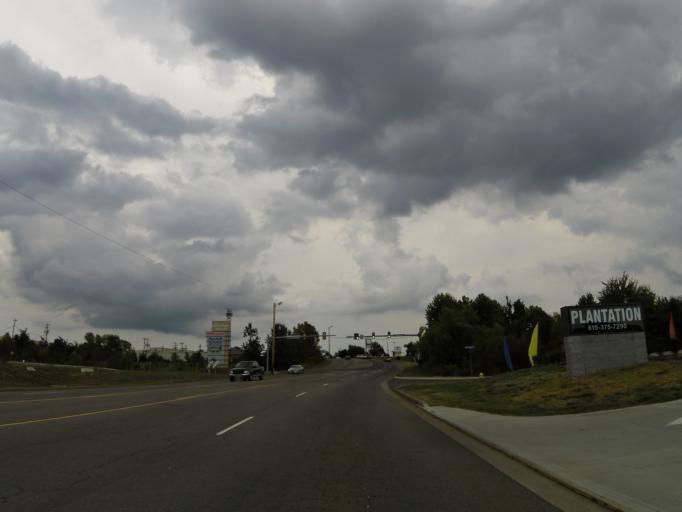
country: US
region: Tennessee
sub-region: Dickson County
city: Dickson
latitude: 36.0633
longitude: -87.3832
